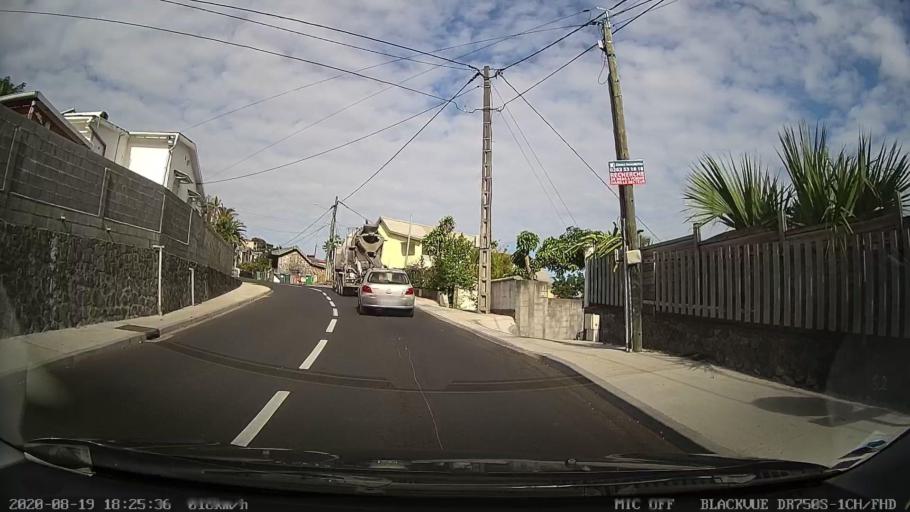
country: RE
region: Reunion
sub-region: Reunion
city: La Possession
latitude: -20.9537
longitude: 55.3498
